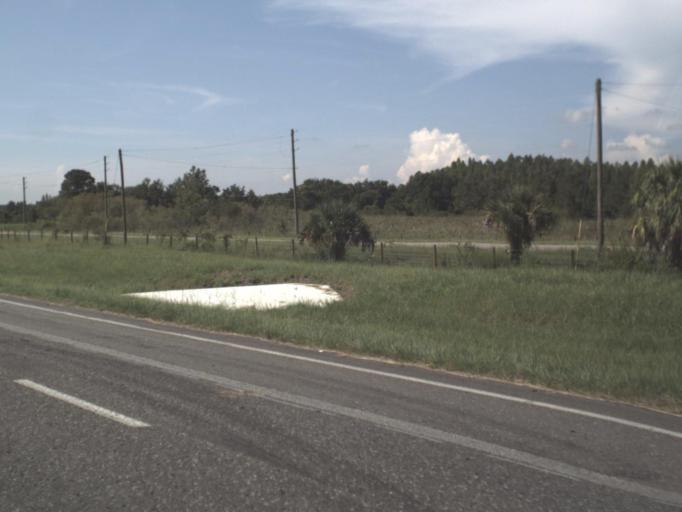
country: US
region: Florida
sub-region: Hillsborough County
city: Pebble Creek
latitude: 28.1405
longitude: -82.3811
